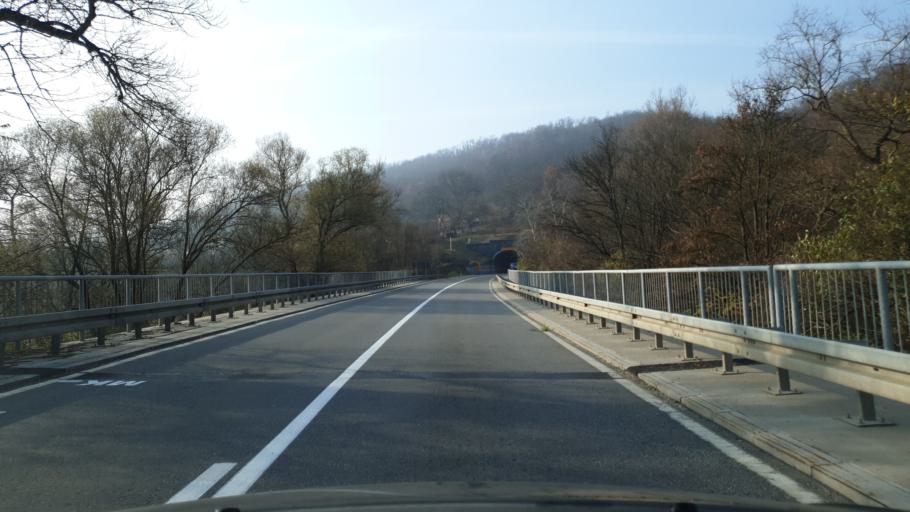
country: RS
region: Central Serbia
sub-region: Zajecarski Okrug
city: Zajecar
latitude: 43.9281
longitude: 22.1369
